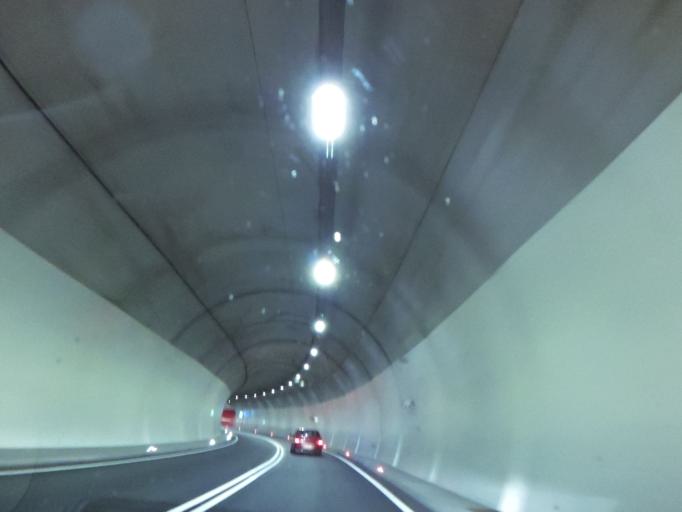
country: IT
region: Trentino-Alto Adige
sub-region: Bolzano
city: Fie Allo Sciliar
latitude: 46.5077
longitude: 11.4887
